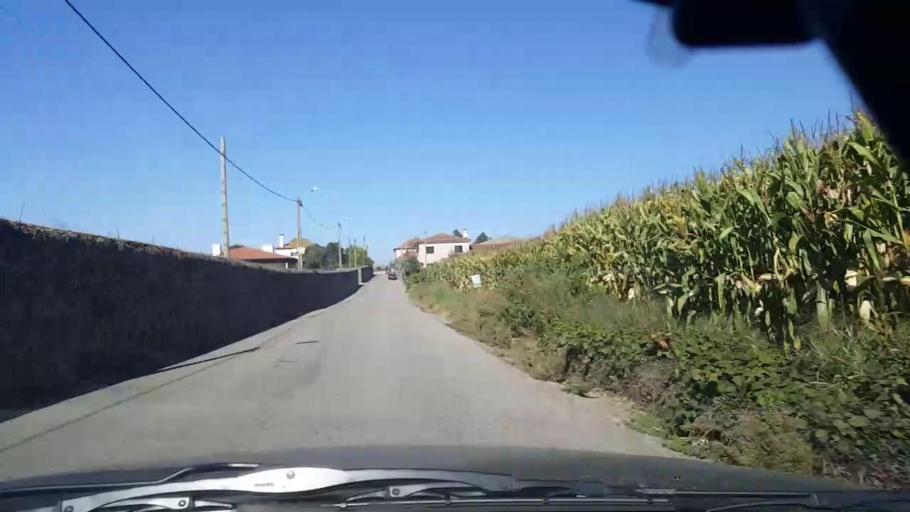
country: PT
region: Porto
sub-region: Vila do Conde
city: Arvore
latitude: 41.3674
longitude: -8.6463
